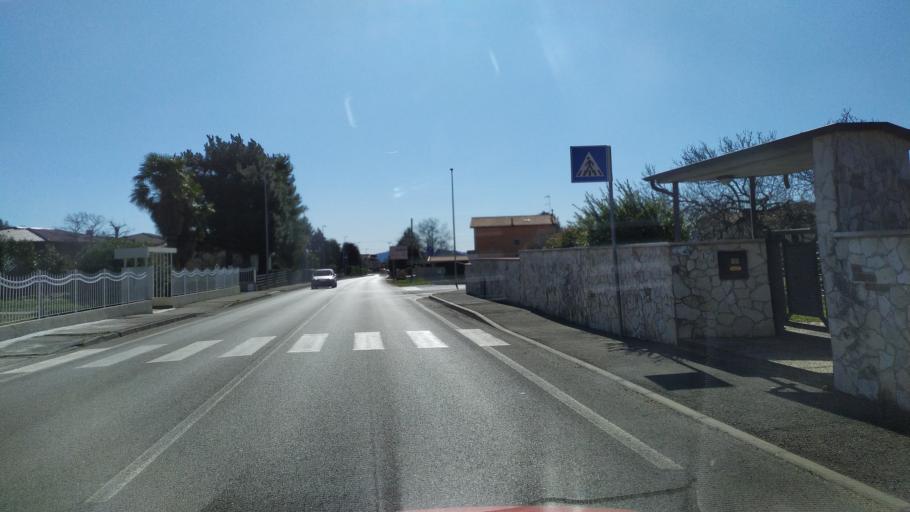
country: IT
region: Veneto
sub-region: Provincia di Vicenza
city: Chiuppano
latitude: 45.7573
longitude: 11.4582
